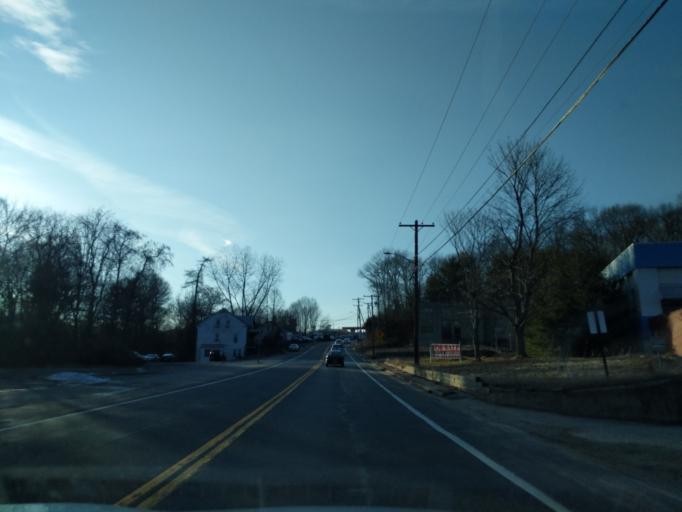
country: US
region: Massachusetts
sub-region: Worcester County
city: Blackstone
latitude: 41.9999
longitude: -71.5530
